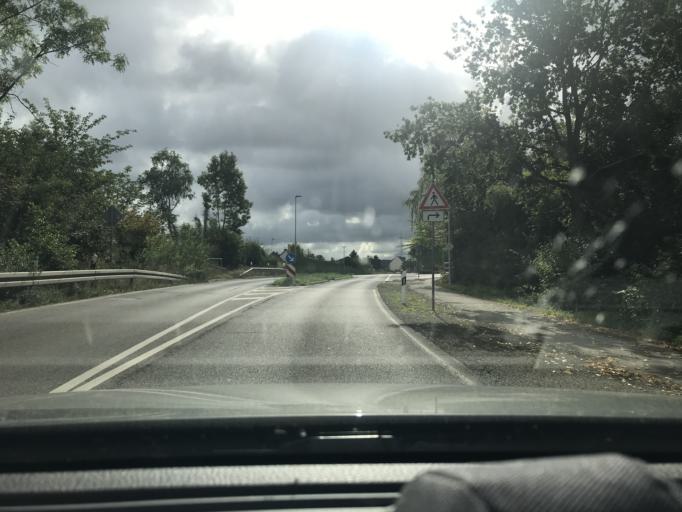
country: DE
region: North Rhine-Westphalia
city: Haan
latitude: 51.2248
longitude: 7.0144
